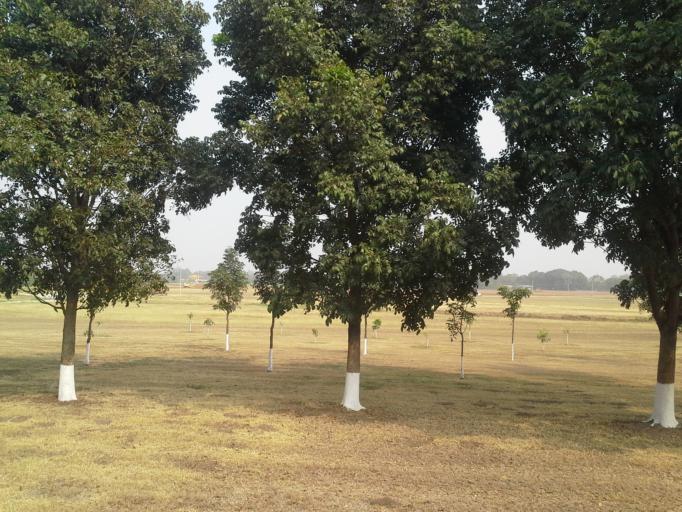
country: IN
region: Telangana
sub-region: Medak
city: Patancheru
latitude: 17.5137
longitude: 78.2741
